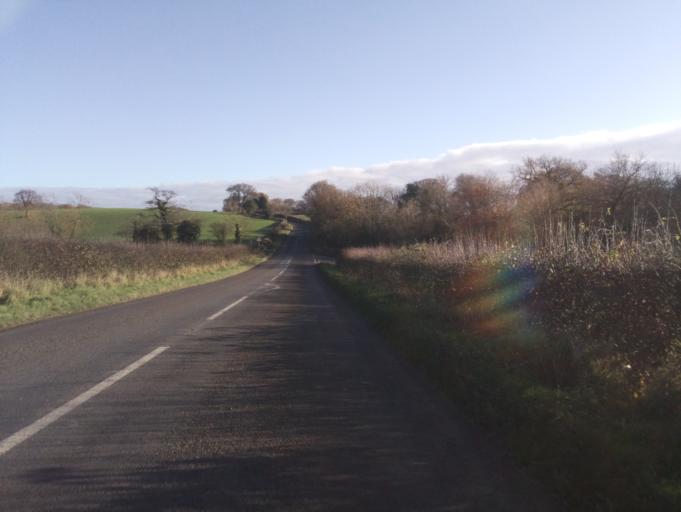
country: GB
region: England
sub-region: Staffordshire
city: Barton under Needwood
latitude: 52.8196
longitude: -1.7770
